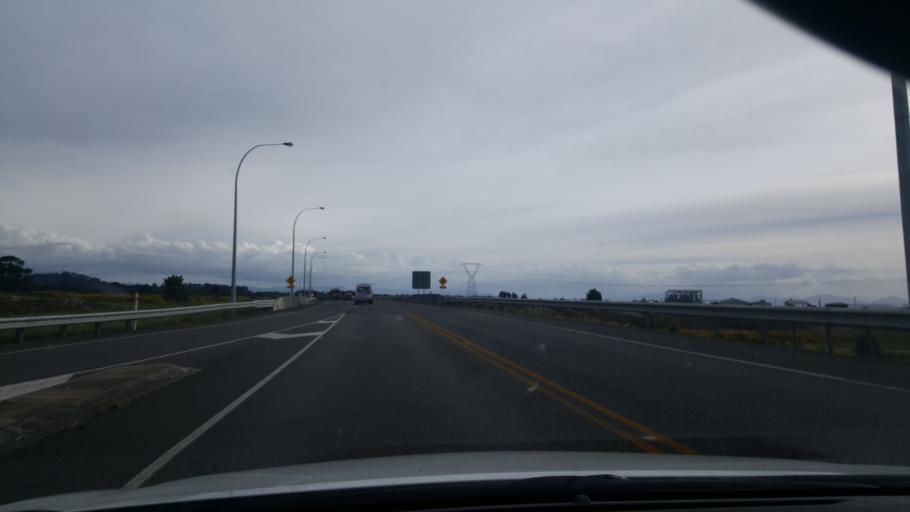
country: NZ
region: Waikato
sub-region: Taupo District
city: Taupo
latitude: -38.6835
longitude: 176.1145
